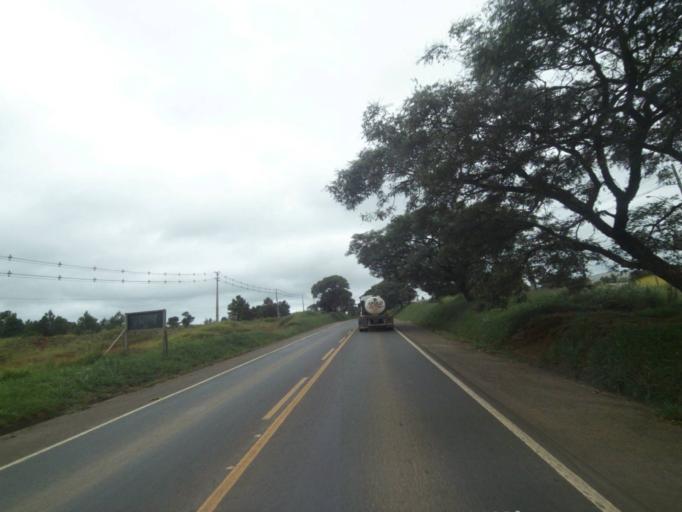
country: BR
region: Parana
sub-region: Telemaco Borba
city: Telemaco Borba
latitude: -24.3533
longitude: -50.6595
